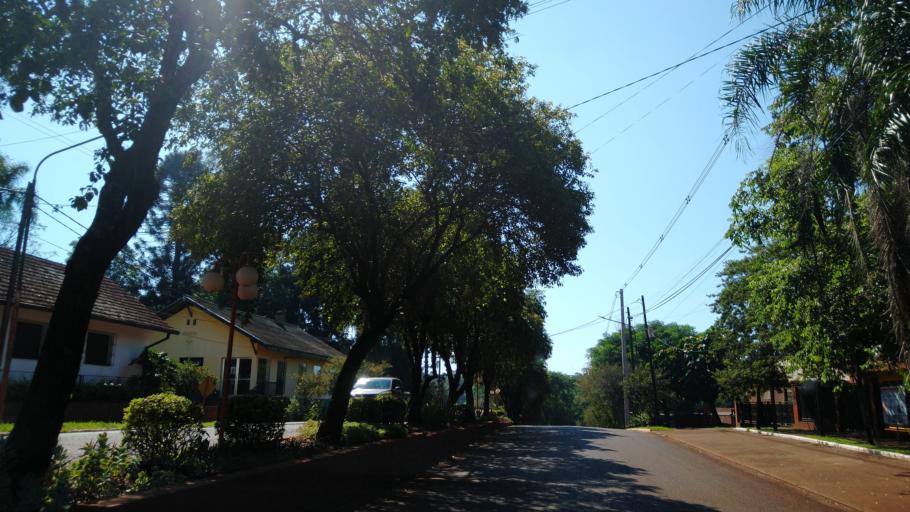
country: AR
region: Misiones
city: Puerto Esperanza
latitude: -26.0227
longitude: -54.6124
